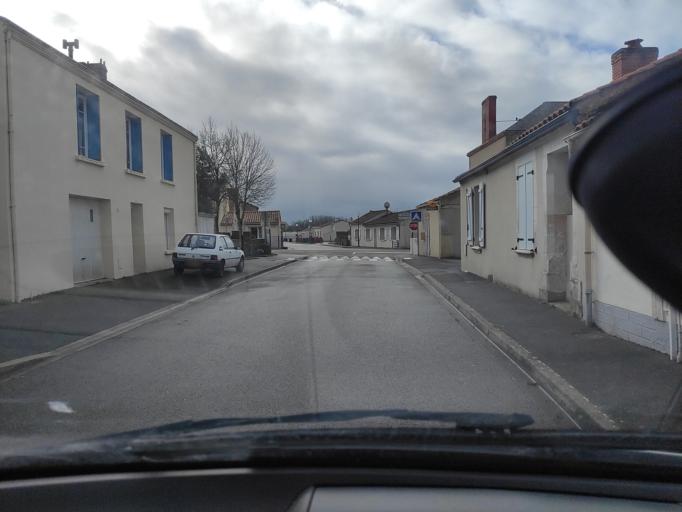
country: FR
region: Pays de la Loire
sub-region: Departement de la Vendee
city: La Boissiere-des-Landes
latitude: 46.5648
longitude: -1.4612
